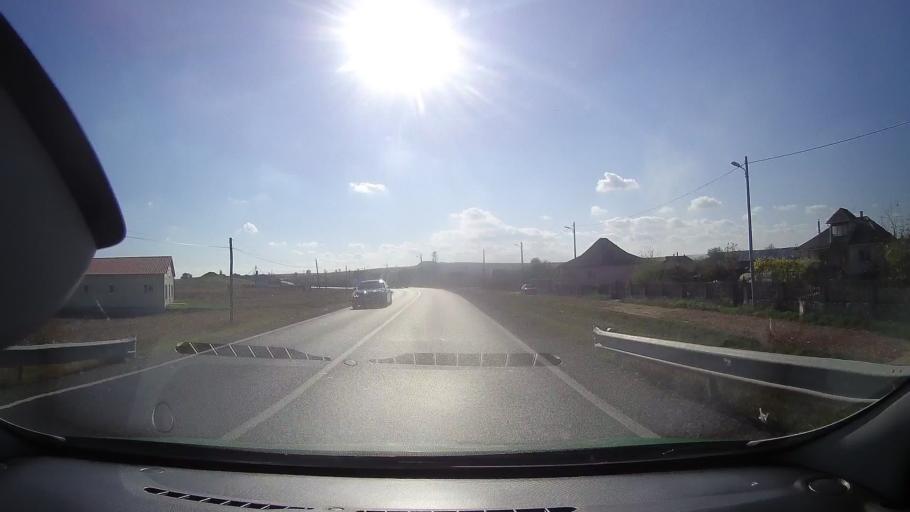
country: RO
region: Tulcea
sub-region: Comuna Baia
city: Baia
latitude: 44.7219
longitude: 28.6794
